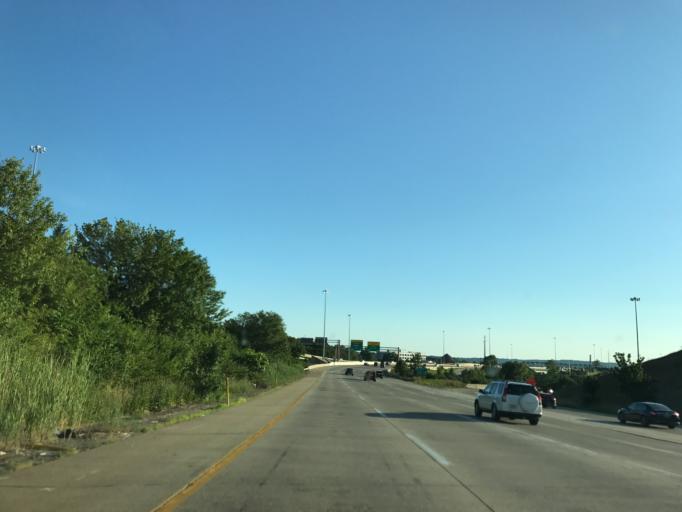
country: US
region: Pennsylvania
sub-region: Montgomery County
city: Plymouth Meeting
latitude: 40.1123
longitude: -75.2783
